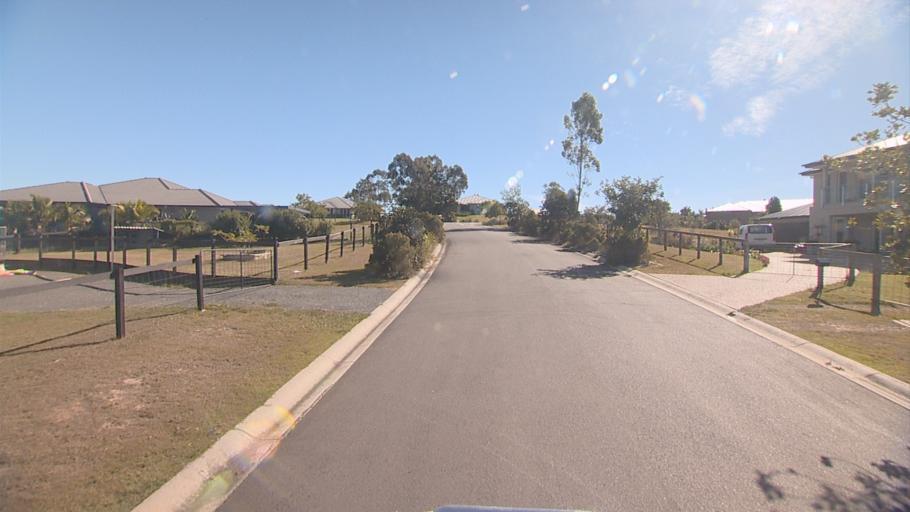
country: AU
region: Queensland
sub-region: Logan
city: North Maclean
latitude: -27.8273
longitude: 152.9844
